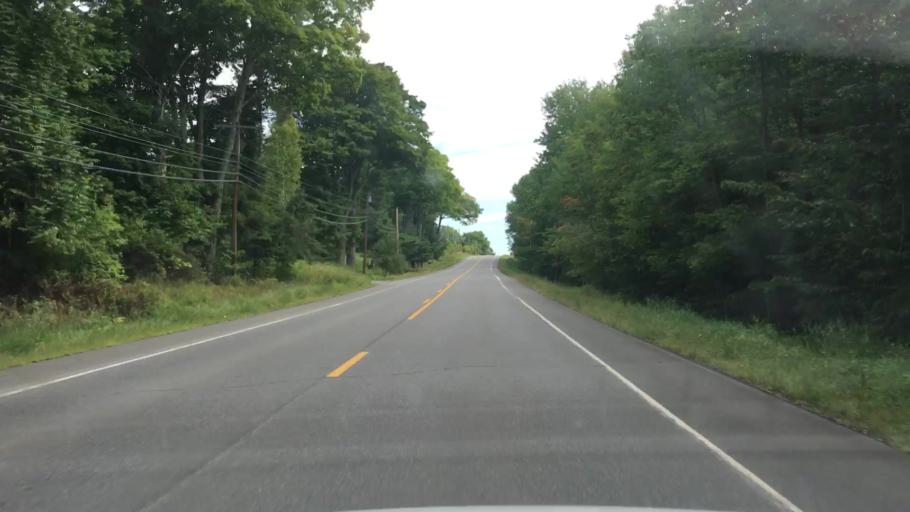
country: US
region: Maine
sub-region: Piscataquis County
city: Brownville
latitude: 45.2273
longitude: -69.1116
